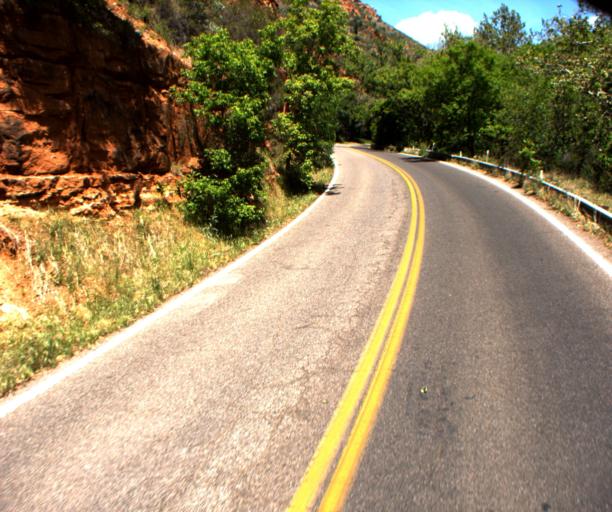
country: US
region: Arizona
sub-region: Coconino County
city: Sedona
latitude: 34.9062
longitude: -111.7277
